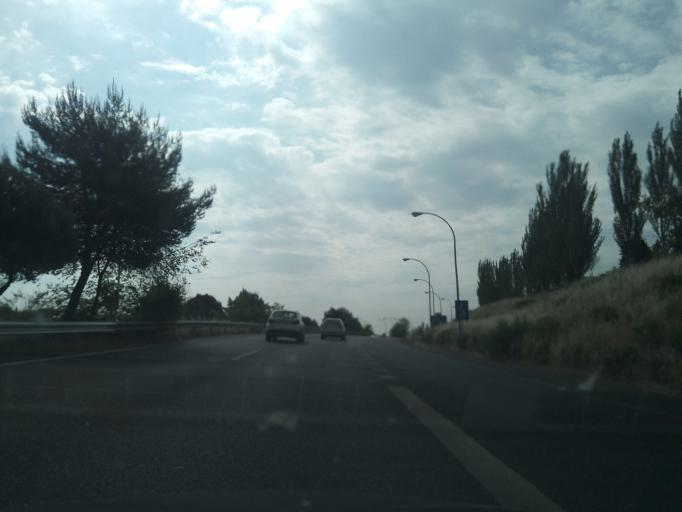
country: ES
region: Madrid
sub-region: Provincia de Madrid
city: Hortaleza
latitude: 40.4800
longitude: -3.6444
